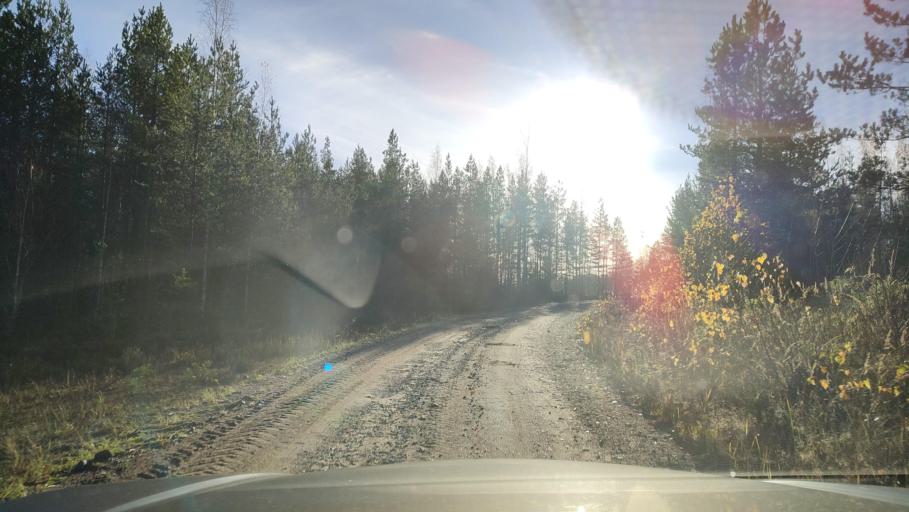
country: FI
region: Southern Ostrobothnia
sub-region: Suupohja
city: Karijoki
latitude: 62.2129
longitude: 21.6279
